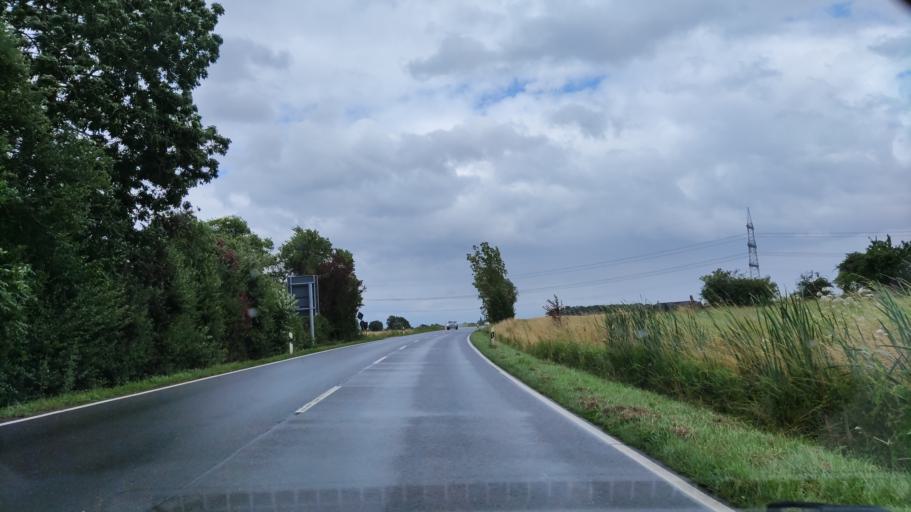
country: DE
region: North Rhine-Westphalia
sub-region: Regierungsbezirk Arnsberg
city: Welver
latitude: 51.6475
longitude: 7.9363
